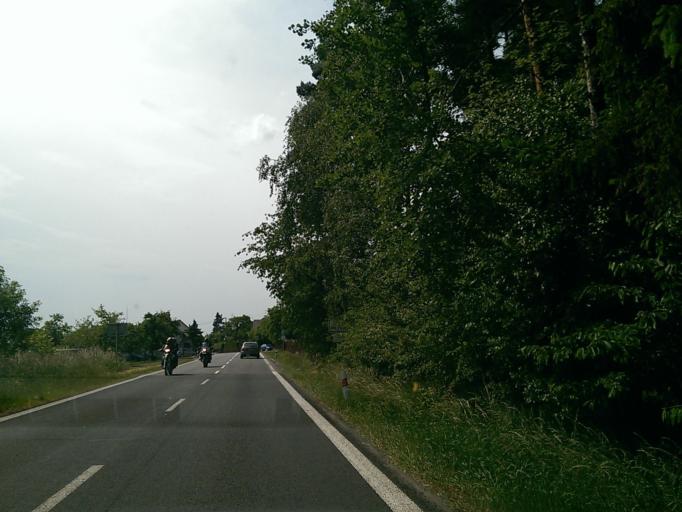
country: CZ
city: Bila Tremesna
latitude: 50.4241
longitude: 15.7378
